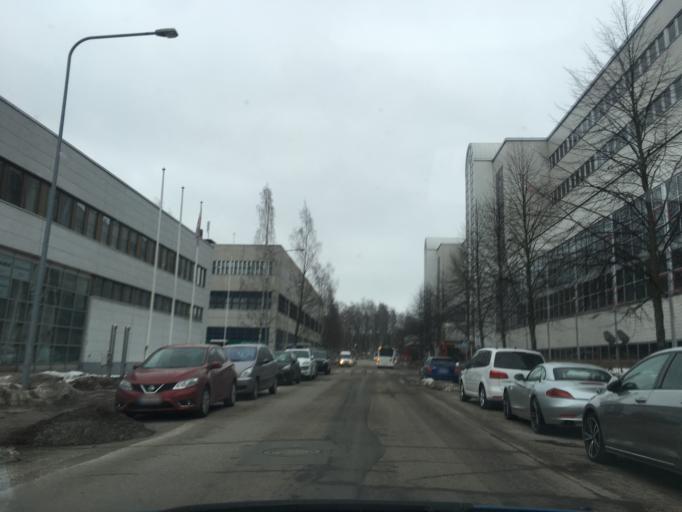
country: FI
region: Uusimaa
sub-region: Helsinki
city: Vantaa
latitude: 60.2099
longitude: 25.0523
